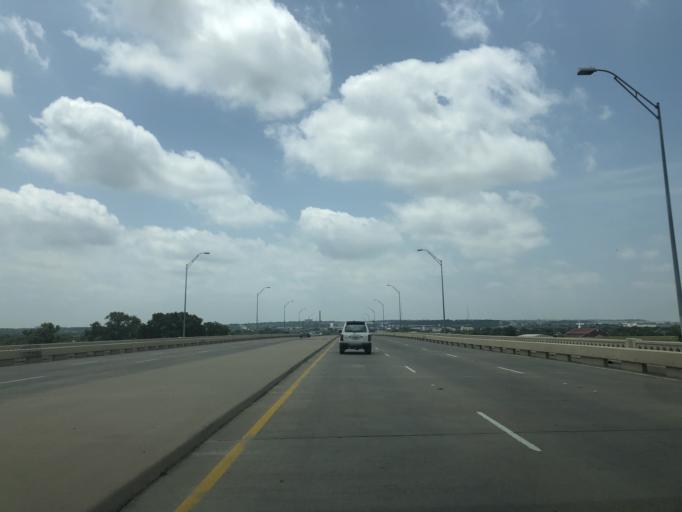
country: US
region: Texas
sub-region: Dallas County
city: Dallas
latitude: 32.7981
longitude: -96.8548
